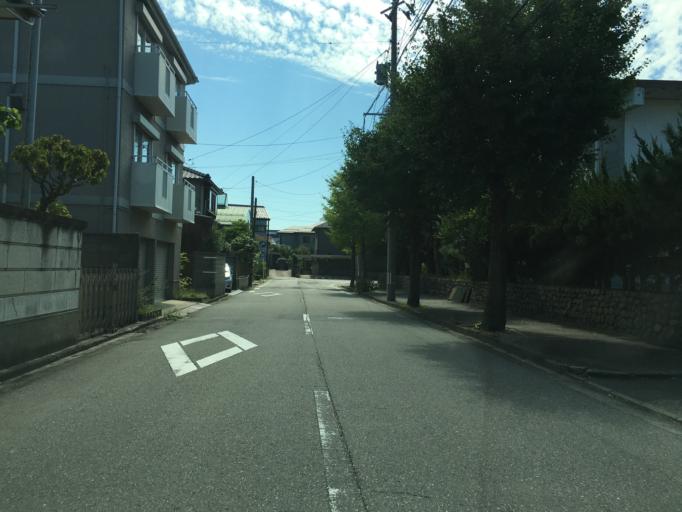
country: JP
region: Niigata
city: Niigata-shi
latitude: 37.9173
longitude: 139.0267
